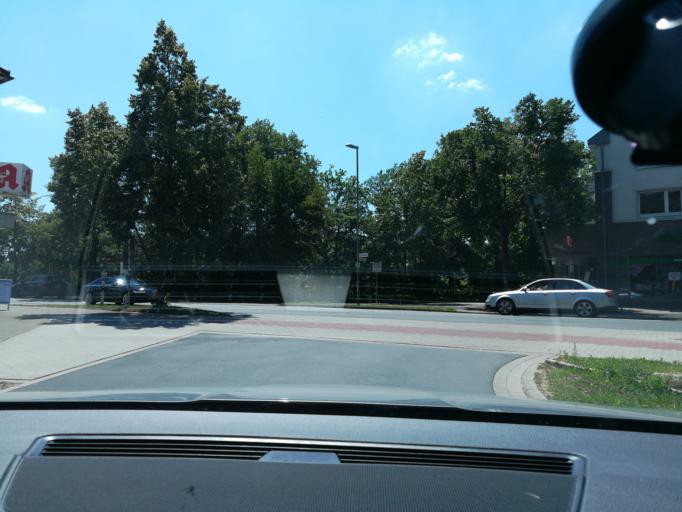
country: DE
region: North Rhine-Westphalia
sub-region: Regierungsbezirk Detmold
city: Minden
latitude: 52.3023
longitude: 8.9072
